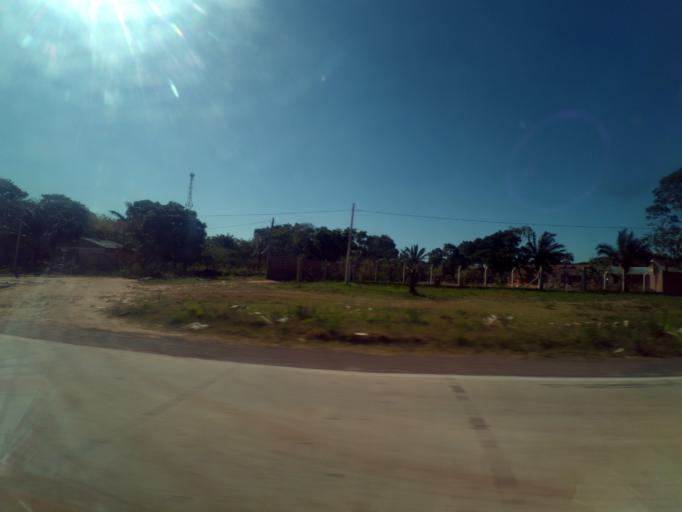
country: BO
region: Santa Cruz
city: Santa Cruz de la Sierra
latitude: -17.7736
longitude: -63.2432
